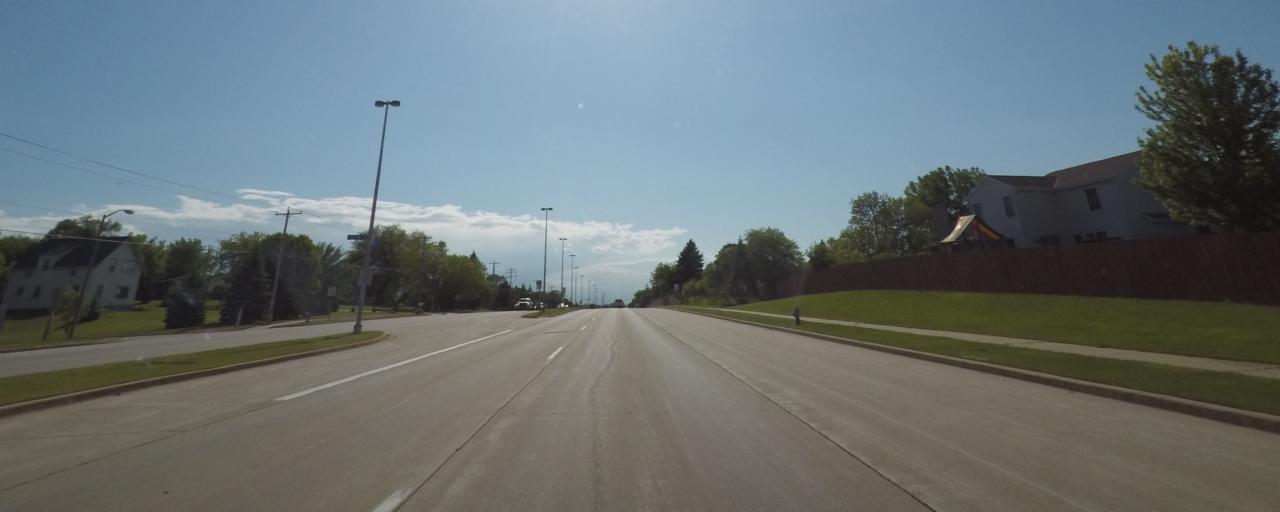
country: US
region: Wisconsin
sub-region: Milwaukee County
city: Greendale
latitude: 42.9160
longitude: -87.9651
